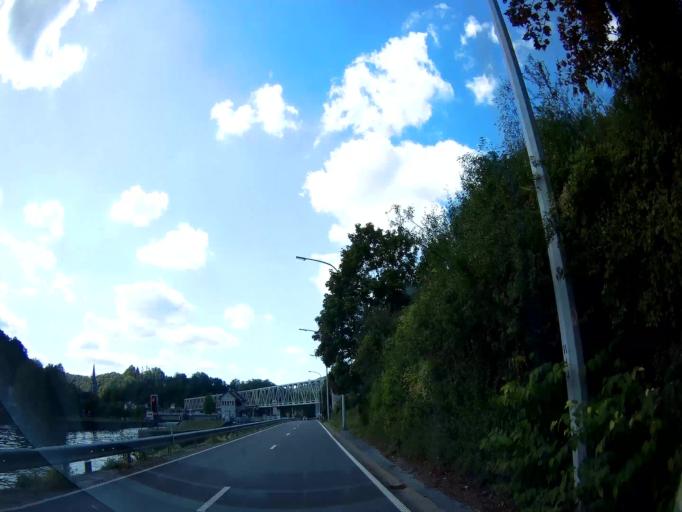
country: BE
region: Wallonia
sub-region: Province de Namur
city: Dinant
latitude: 50.2405
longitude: 4.9121
